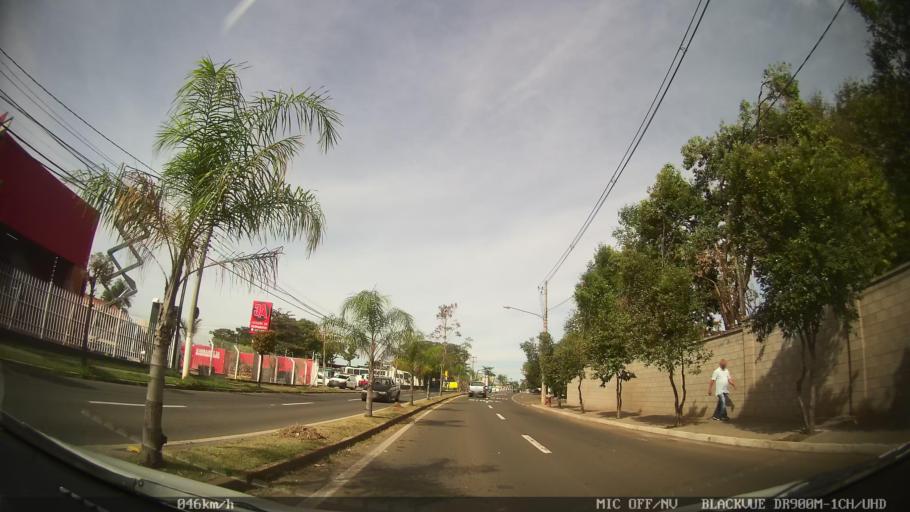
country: BR
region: Sao Paulo
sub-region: Piracicaba
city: Piracicaba
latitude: -22.7511
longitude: -47.6370
